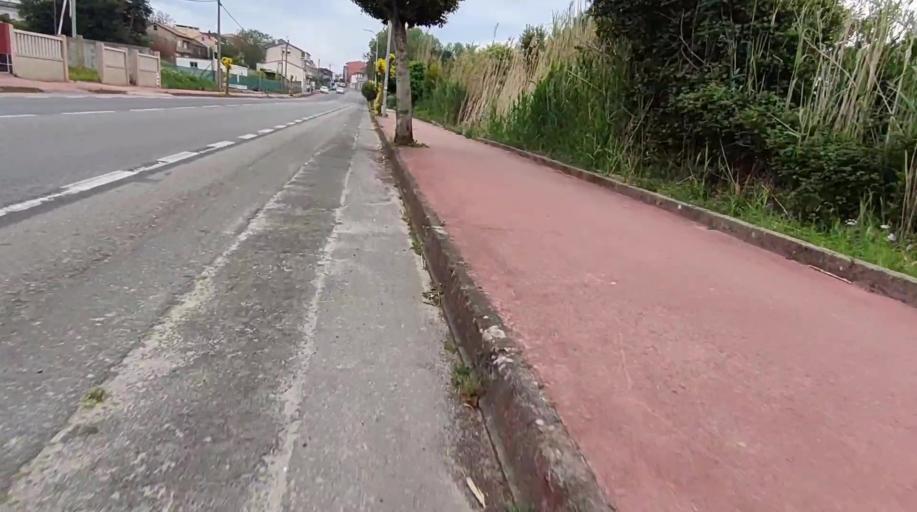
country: ES
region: Galicia
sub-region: Provincia da Coruna
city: Boiro
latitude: 42.6286
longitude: -8.8740
